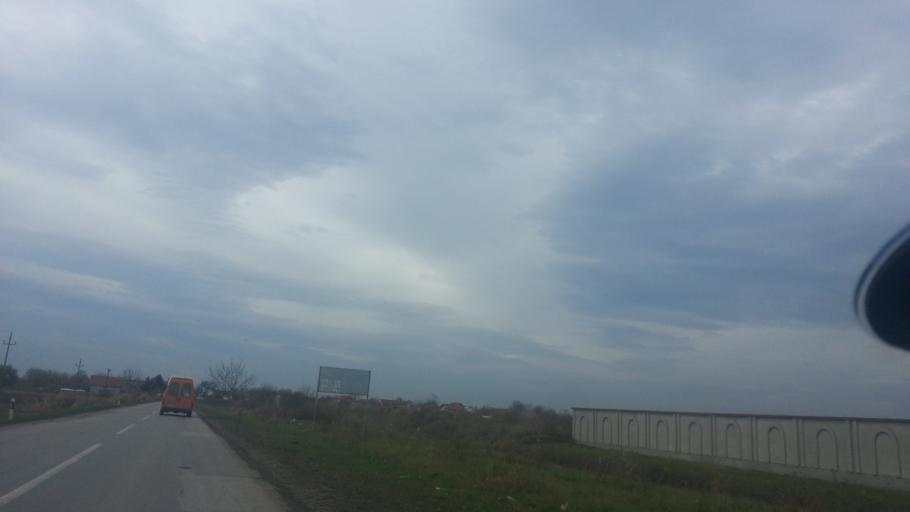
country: RS
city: Golubinci
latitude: 44.9806
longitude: 20.0853
